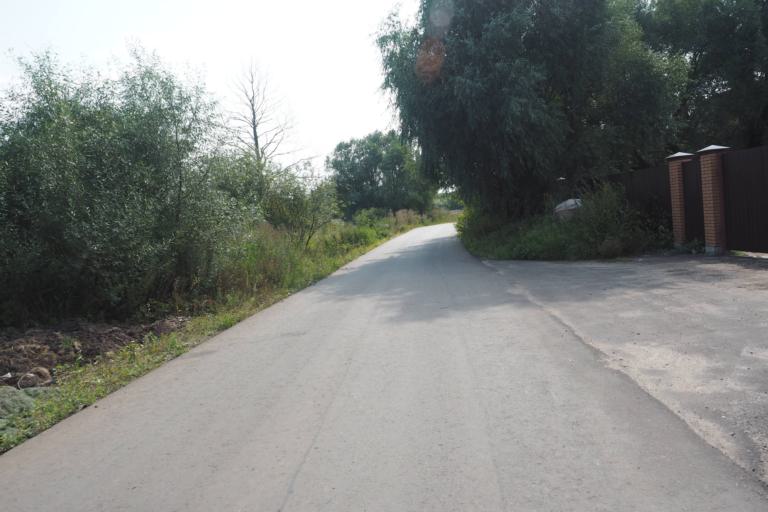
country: RU
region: Moskovskaya
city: Ramenskoye
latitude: 55.5483
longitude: 38.2933
